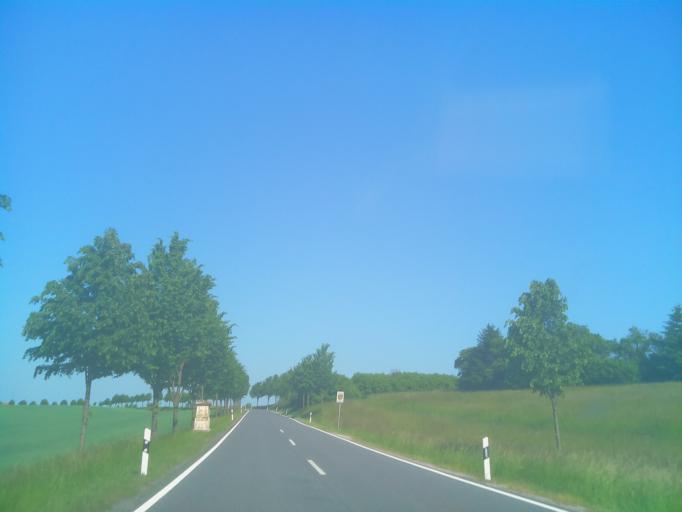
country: DE
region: Thuringia
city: Pennewitz
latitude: 50.6602
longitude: 11.0625
